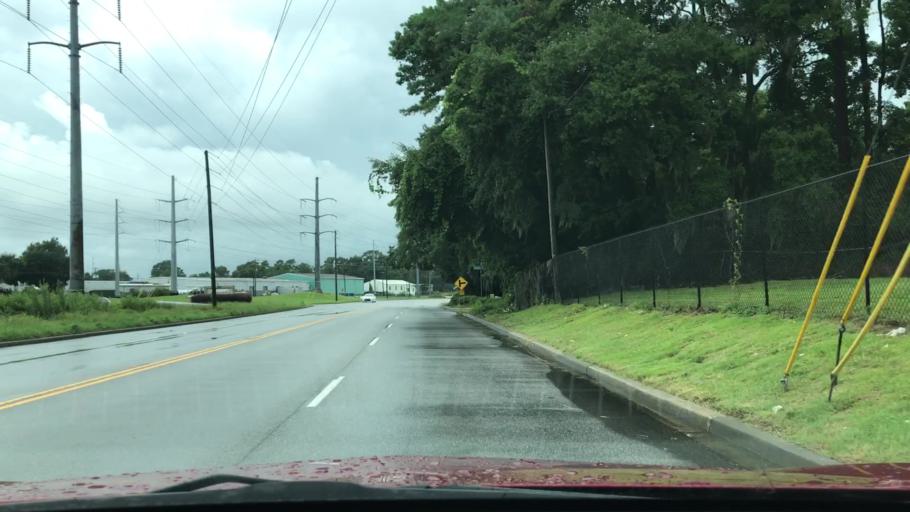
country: US
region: South Carolina
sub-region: Charleston County
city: North Charleston
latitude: 32.8469
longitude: -79.9992
